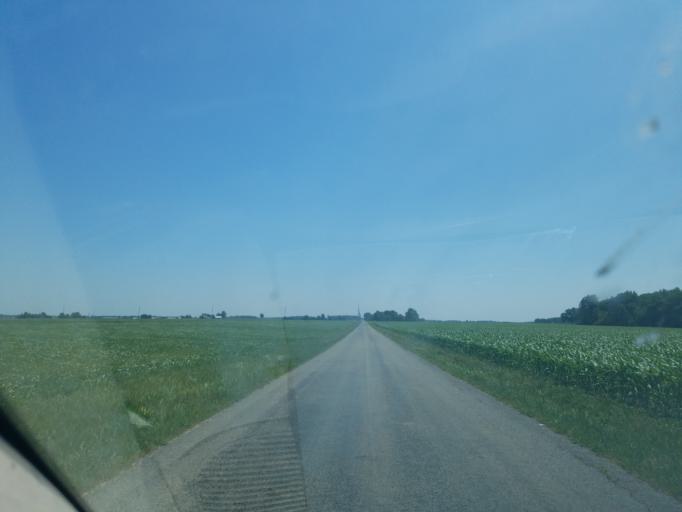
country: US
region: Ohio
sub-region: Mercer County
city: Rockford
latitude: 40.6694
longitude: -84.6971
